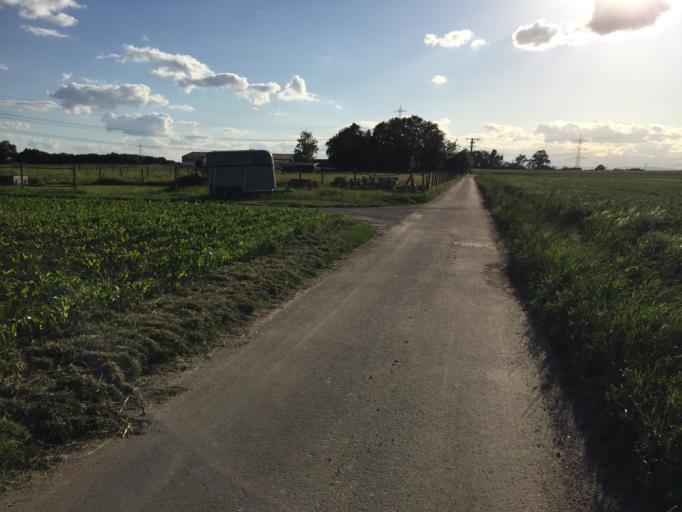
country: DE
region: Hesse
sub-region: Regierungsbezirk Darmstadt
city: Niederdorfelden
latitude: 50.2091
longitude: 8.7908
